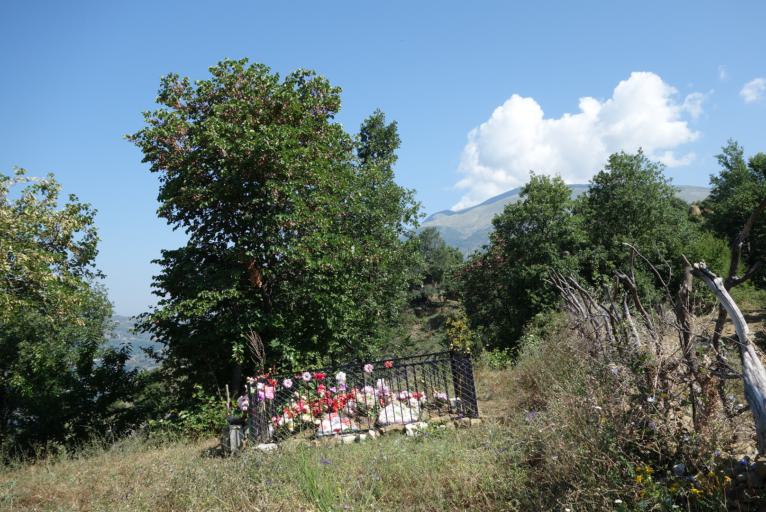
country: AL
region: Berat
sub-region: Rrethi i Skraparit
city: Bogove
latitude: 40.5569
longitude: 20.1644
